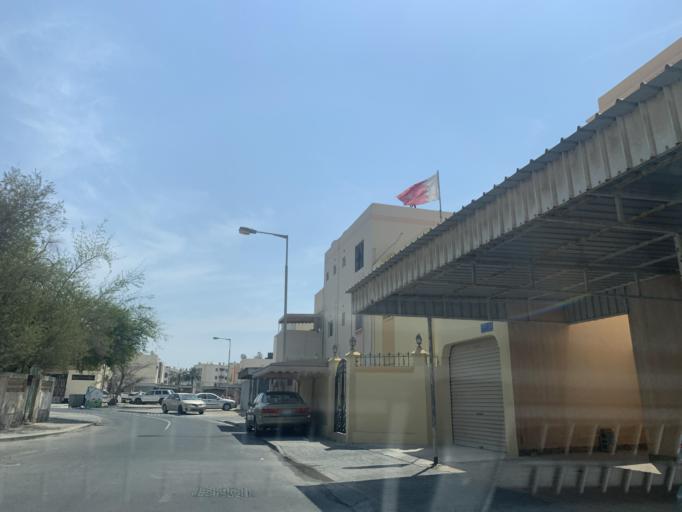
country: BH
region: Central Governorate
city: Madinat Hamad
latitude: 26.1355
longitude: 50.5011
